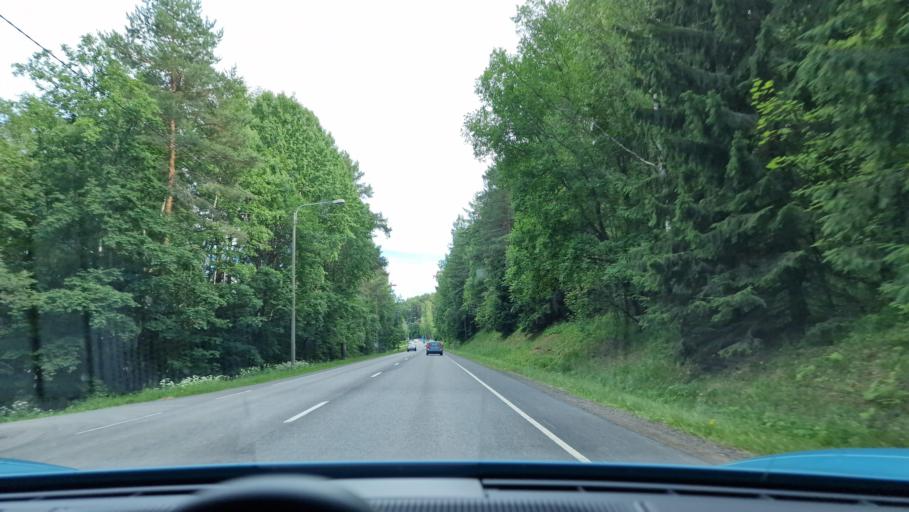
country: FI
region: Pirkanmaa
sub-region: Tampere
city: Kangasala
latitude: 61.4232
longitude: 24.1385
